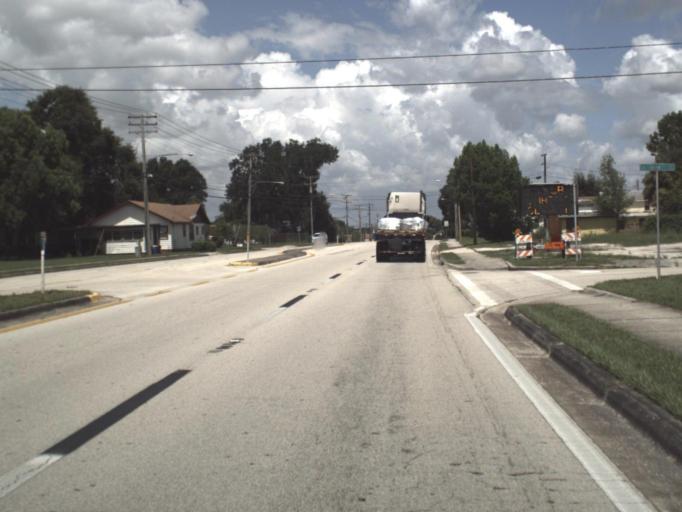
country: US
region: Florida
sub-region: Polk County
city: Bartow
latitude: 27.8885
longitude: -81.8281
